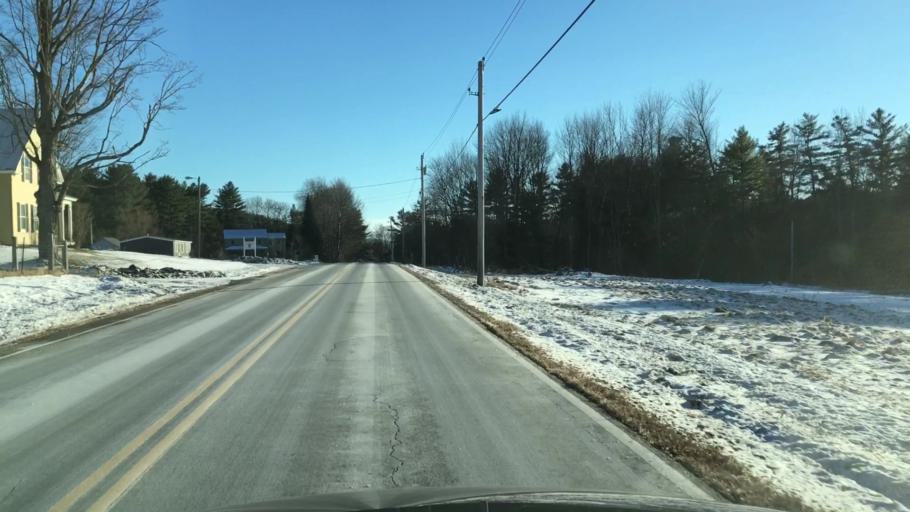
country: US
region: New Hampshire
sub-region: Grafton County
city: Woodsville
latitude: 44.1963
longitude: -72.0569
